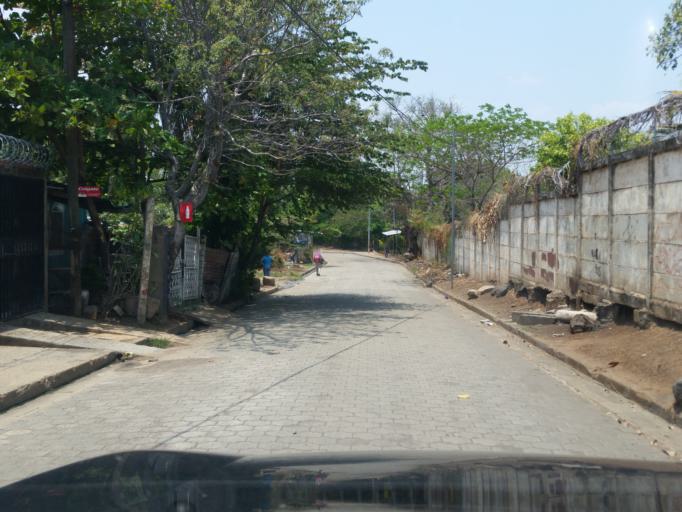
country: NI
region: Granada
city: Granada
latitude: 11.9204
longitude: -85.9627
